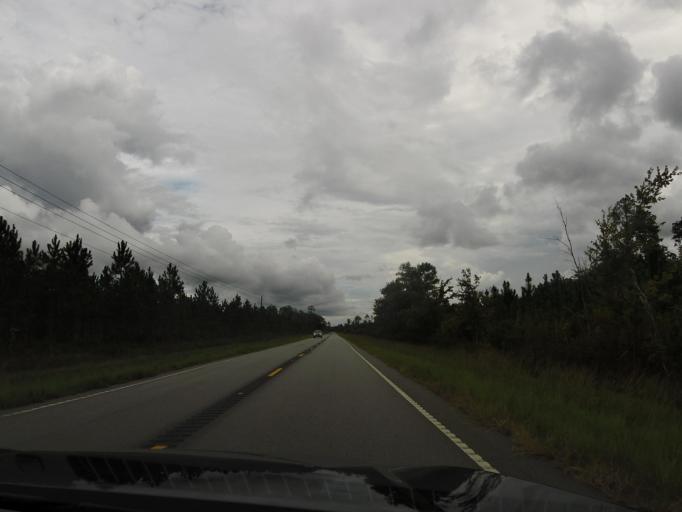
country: US
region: Florida
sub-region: Baker County
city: Macclenny
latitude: 30.5219
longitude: -82.1506
